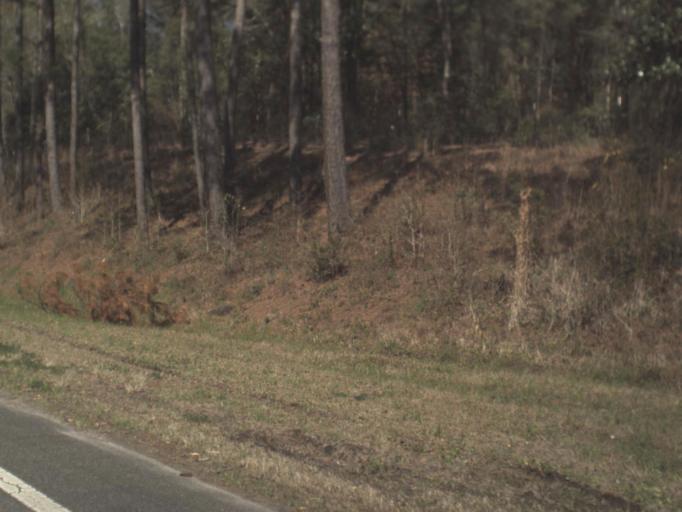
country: US
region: Florida
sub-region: Gadsden County
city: Quincy
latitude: 30.5926
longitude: -84.5196
